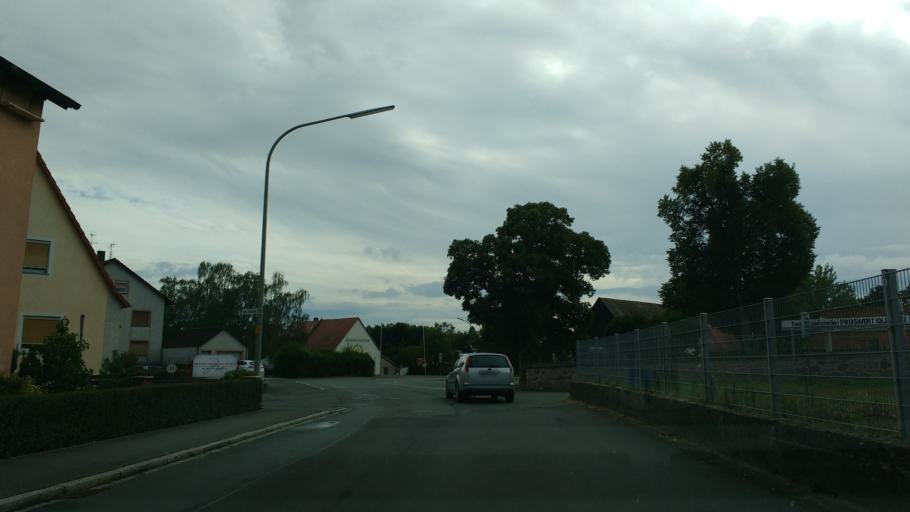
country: DE
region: Bavaria
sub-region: Upper Franconia
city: Schlusselfeld
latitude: 49.7585
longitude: 10.6149
